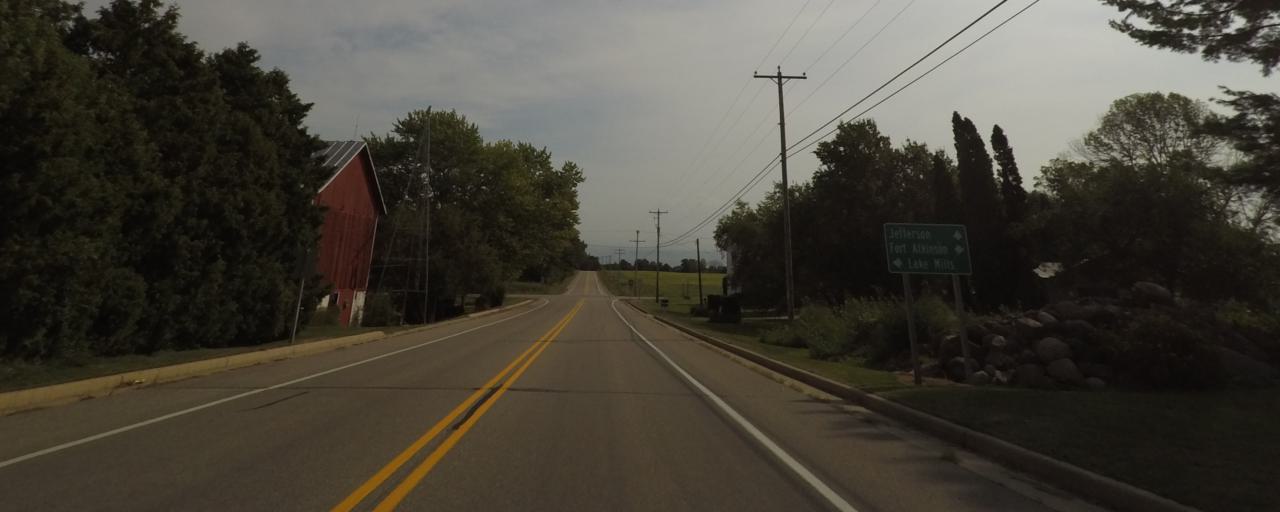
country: US
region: Wisconsin
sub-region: Jefferson County
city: Jefferson
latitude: 42.9916
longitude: -88.8440
